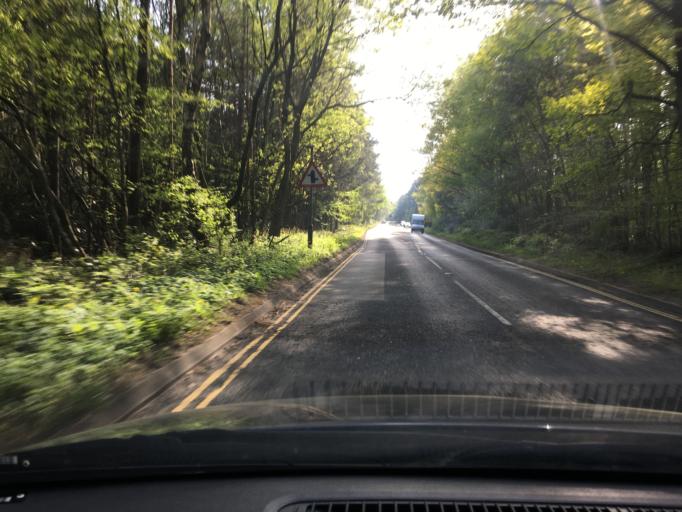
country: GB
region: England
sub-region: Bracknell Forest
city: Bracknell
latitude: 51.3898
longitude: -0.7370
